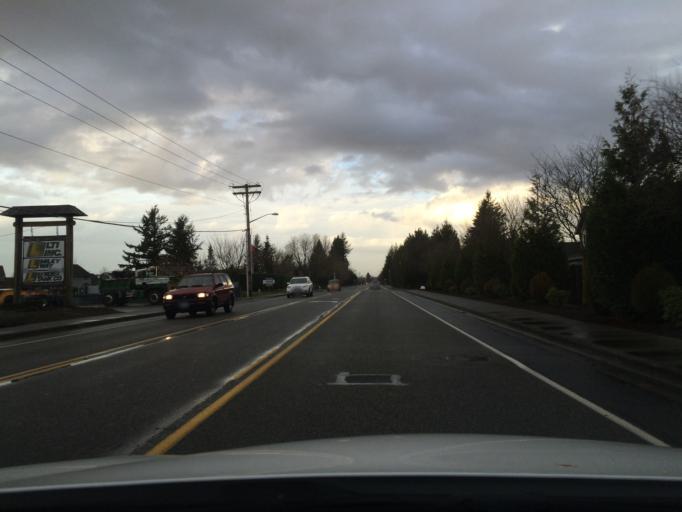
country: US
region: Washington
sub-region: Whatcom County
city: Lynden
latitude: 48.9548
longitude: -122.4522
